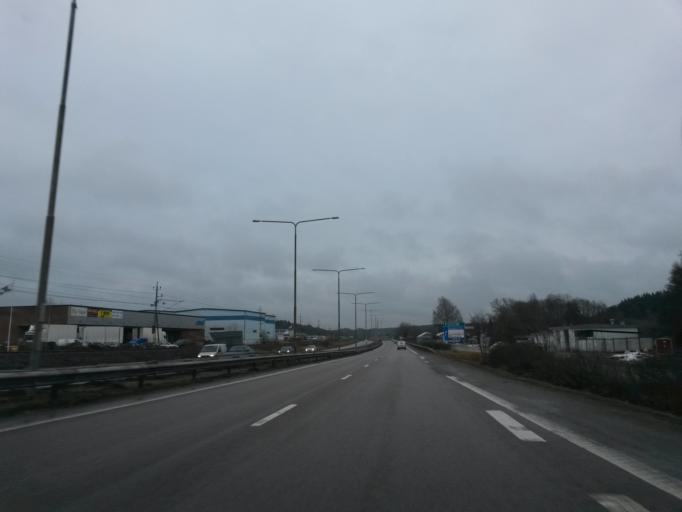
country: SE
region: Vaestra Goetaland
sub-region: Uddevalla Kommun
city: Uddevalla
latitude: 58.3536
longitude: 11.9679
